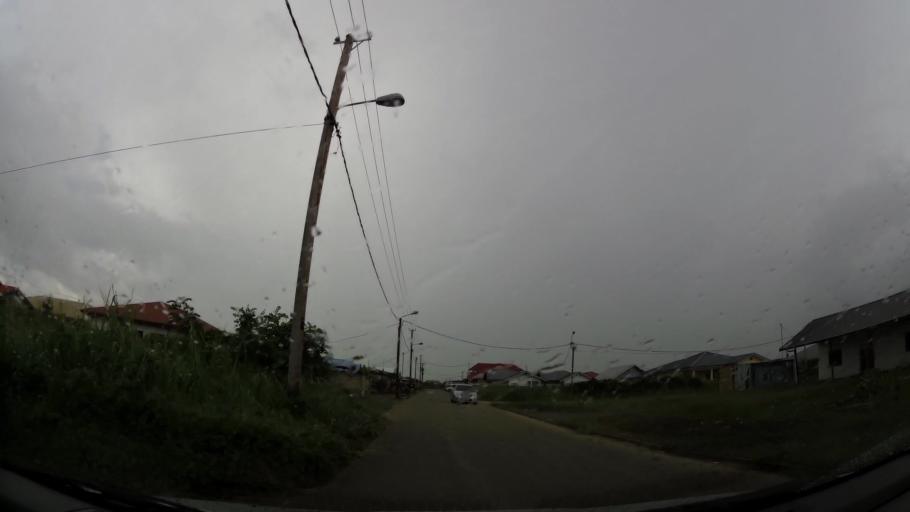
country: SR
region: Commewijne
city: Nieuw Amsterdam
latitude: 5.8549
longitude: -55.1160
